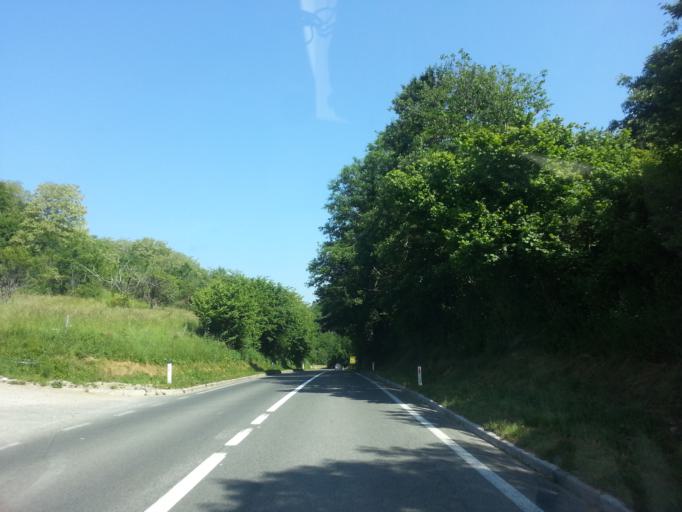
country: SI
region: Ilirska Bistrica
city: Ilirska Bistrica
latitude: 45.5102
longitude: 14.2583
